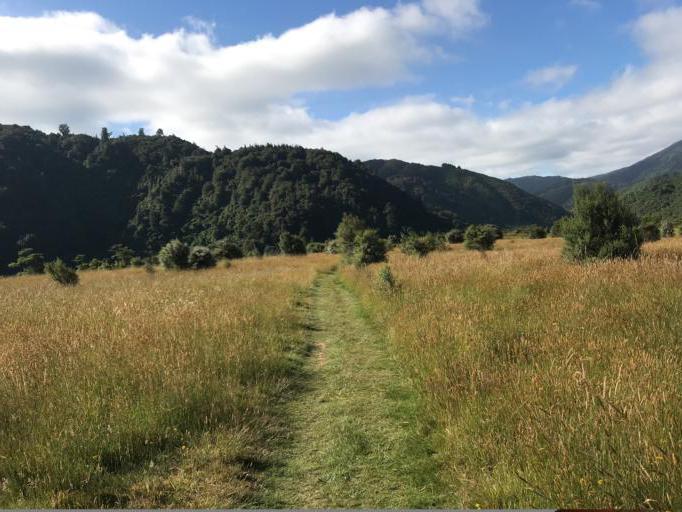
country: NZ
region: Wellington
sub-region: Kapiti Coast District
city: Otaki
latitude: -40.8741
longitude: 175.2348
